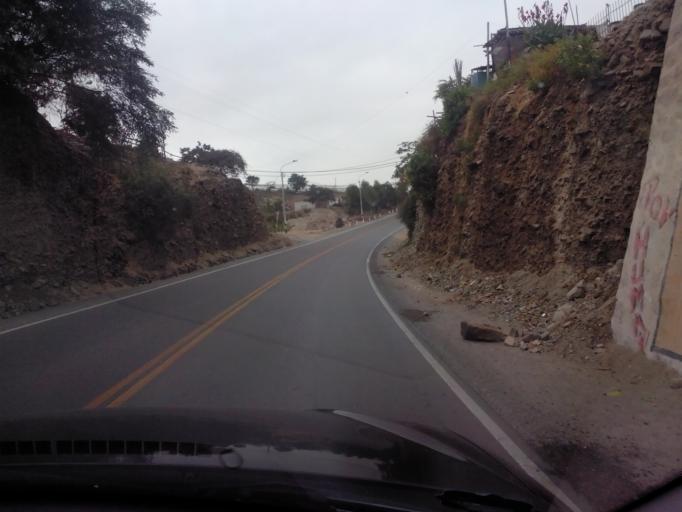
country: PE
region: Ica
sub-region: Provincia de Pisco
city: Humay
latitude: -13.7269
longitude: -75.9411
